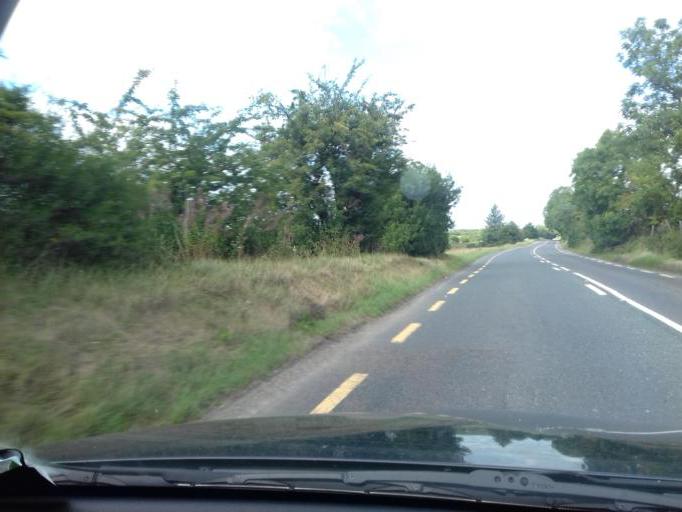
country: IE
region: Leinster
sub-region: Wicklow
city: Valleymount
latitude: 53.0556
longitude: -6.6269
